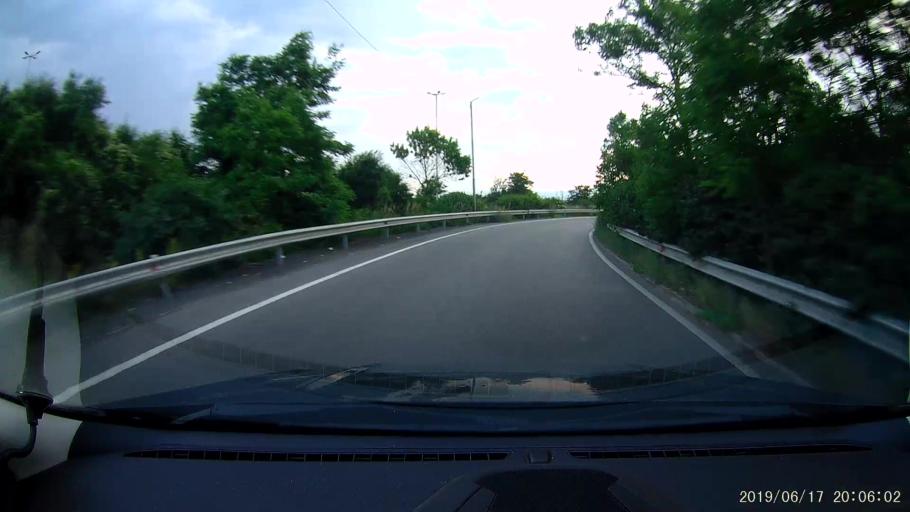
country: BG
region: Sofia-Capital
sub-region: Stolichna Obshtina
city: Sofia
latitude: 42.6349
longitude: 23.4492
